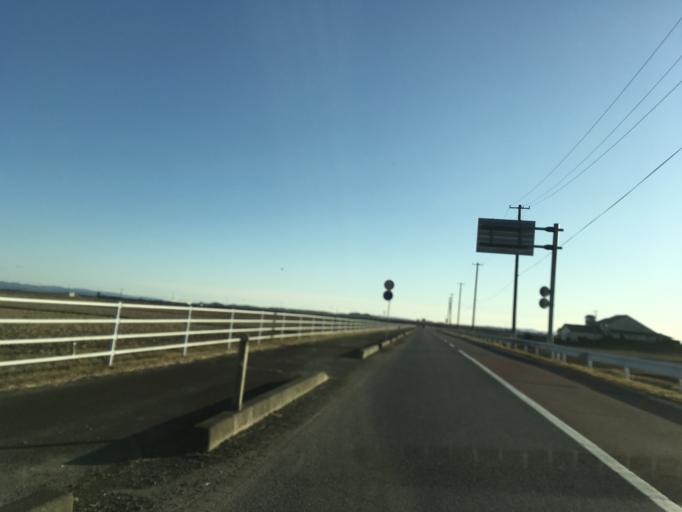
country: JP
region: Iwate
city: Ichinoseki
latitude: 38.7515
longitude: 141.1644
